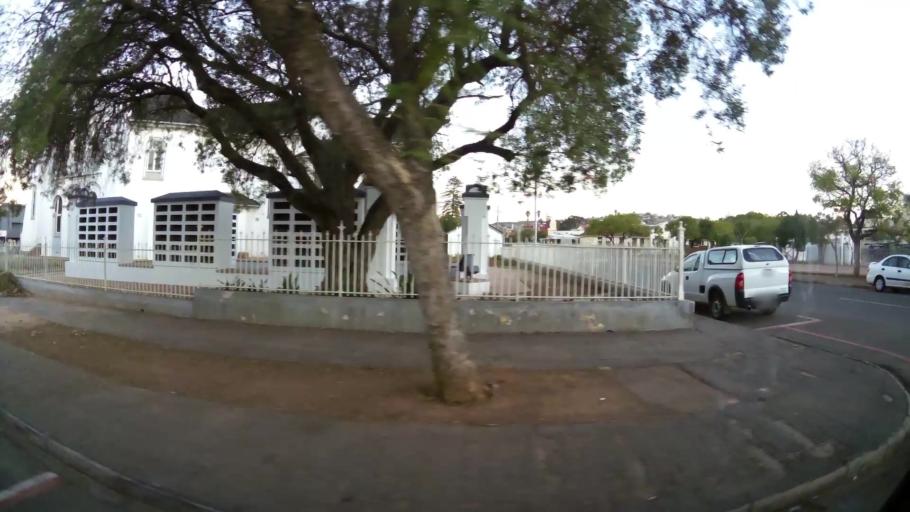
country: ZA
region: Western Cape
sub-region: Eden District Municipality
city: Riversdale
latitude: -34.0906
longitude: 21.2601
